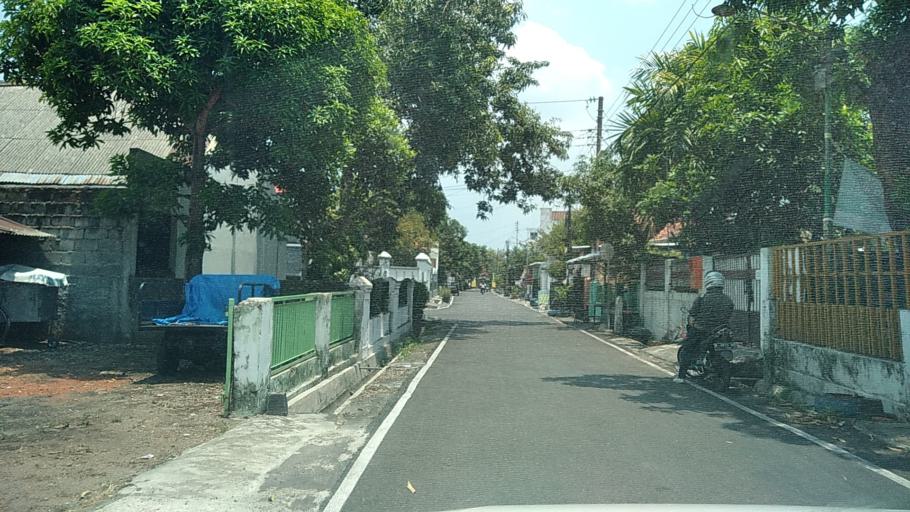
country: ID
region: Central Java
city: Semarang
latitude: -7.0044
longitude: 110.4406
